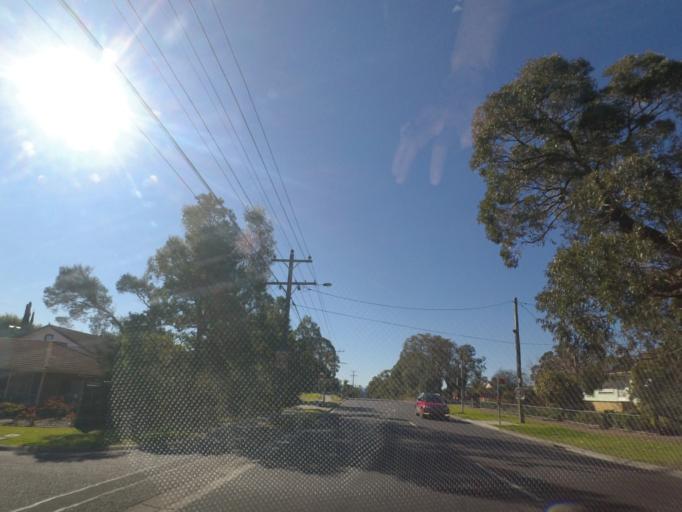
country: AU
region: Victoria
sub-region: Maroondah
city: Croydon Hills
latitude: -37.7813
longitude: 145.2743
